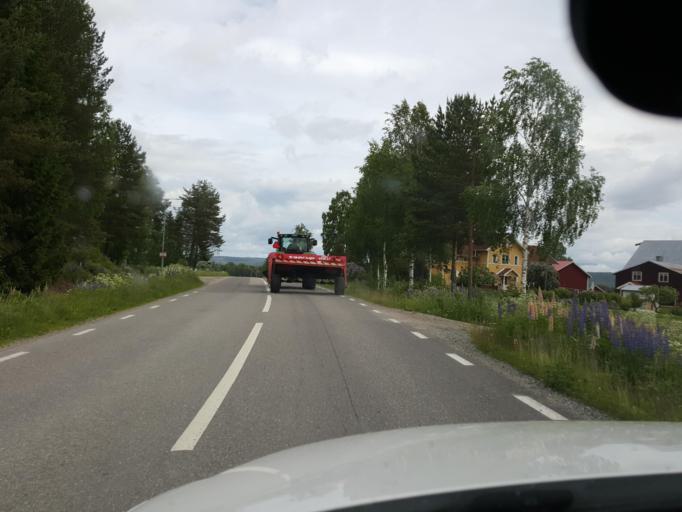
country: SE
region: Gaevleborg
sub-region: Ljusdals Kommun
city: Farila
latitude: 61.8070
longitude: 15.7343
